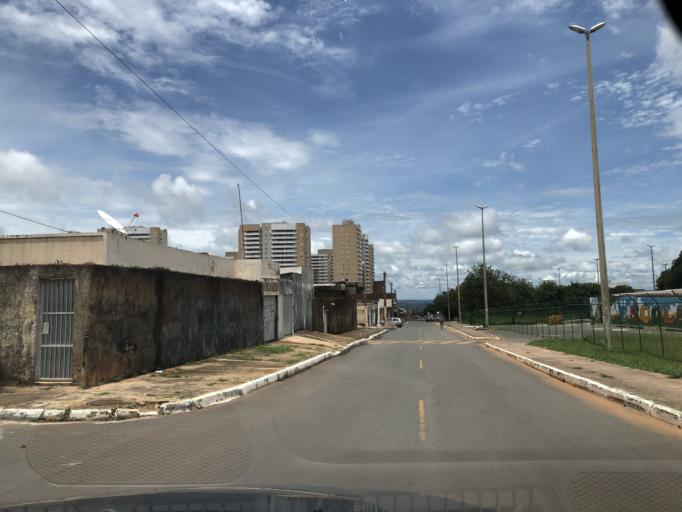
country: BR
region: Federal District
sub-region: Brasilia
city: Brasilia
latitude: -15.8156
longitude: -48.1200
